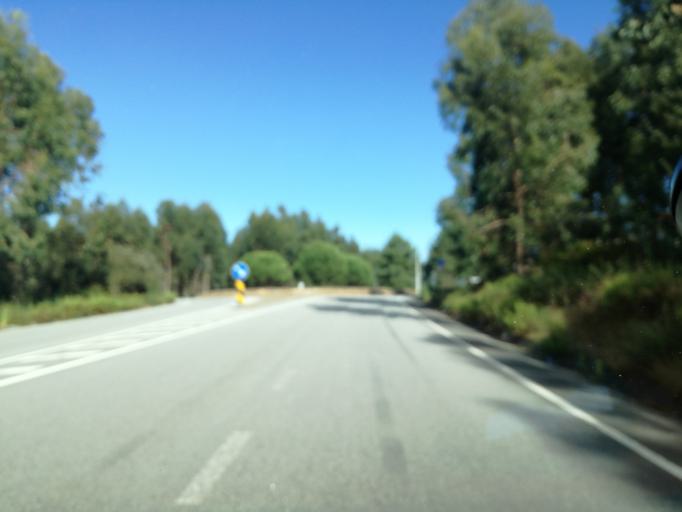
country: PT
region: Porto
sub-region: Pacos de Ferreira
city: Seroa
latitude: 41.2704
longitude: -8.4357
